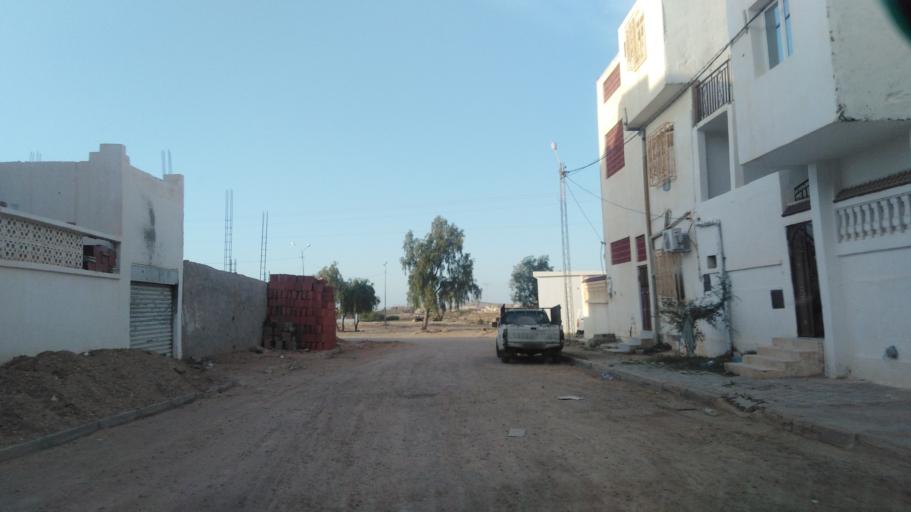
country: TN
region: Tataouine
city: Tataouine
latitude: 32.9429
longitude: 10.4580
